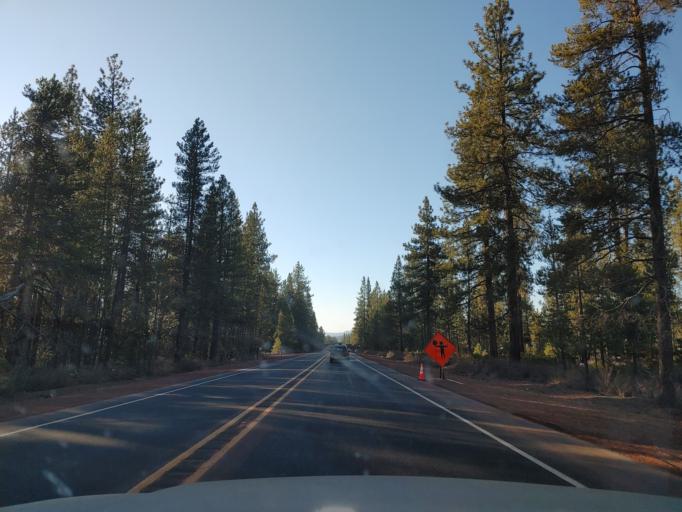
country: US
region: Oregon
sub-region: Deschutes County
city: La Pine
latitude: 43.3745
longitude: -121.7952
